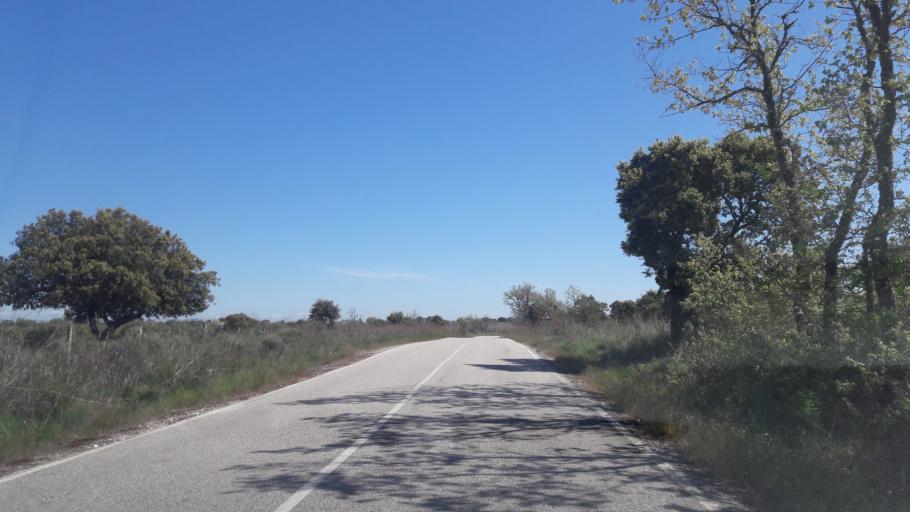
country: ES
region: Castille and Leon
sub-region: Provincia de Salamanca
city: Villarmuerto
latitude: 41.0436
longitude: -6.3896
